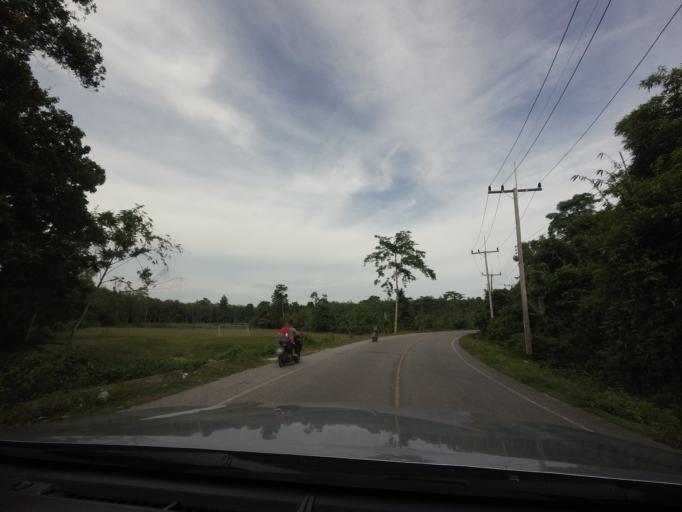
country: TH
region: Narathiwat
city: Rueso
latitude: 6.3468
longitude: 101.4789
